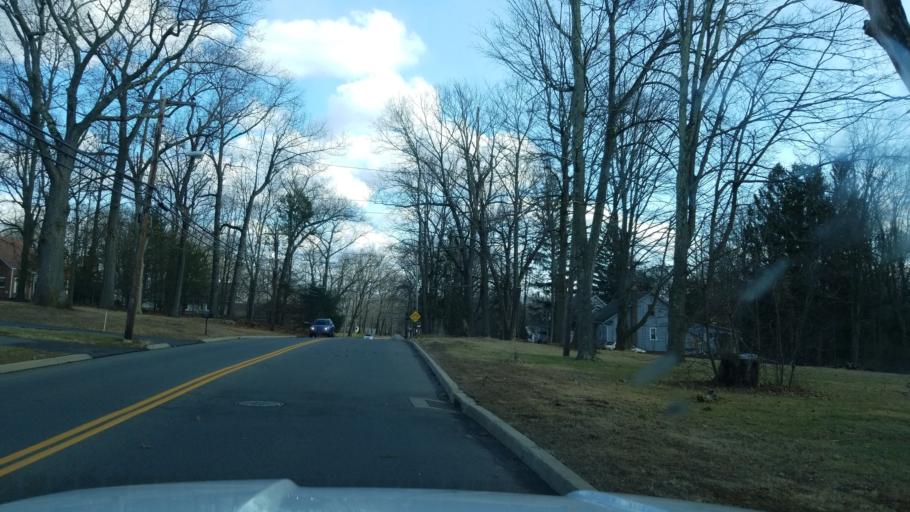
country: US
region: Connecticut
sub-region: Middlesex County
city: Middletown
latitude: 41.5634
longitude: -72.6994
